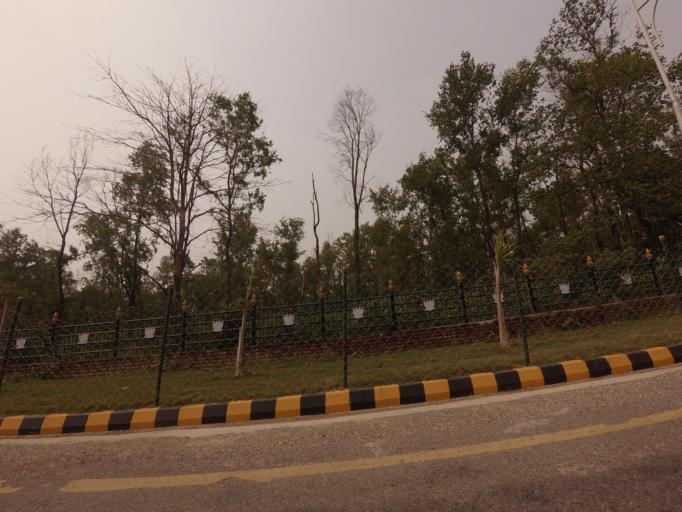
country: IN
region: Uttar Pradesh
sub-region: Maharajganj
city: Nautanwa
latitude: 27.4915
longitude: 83.2710
